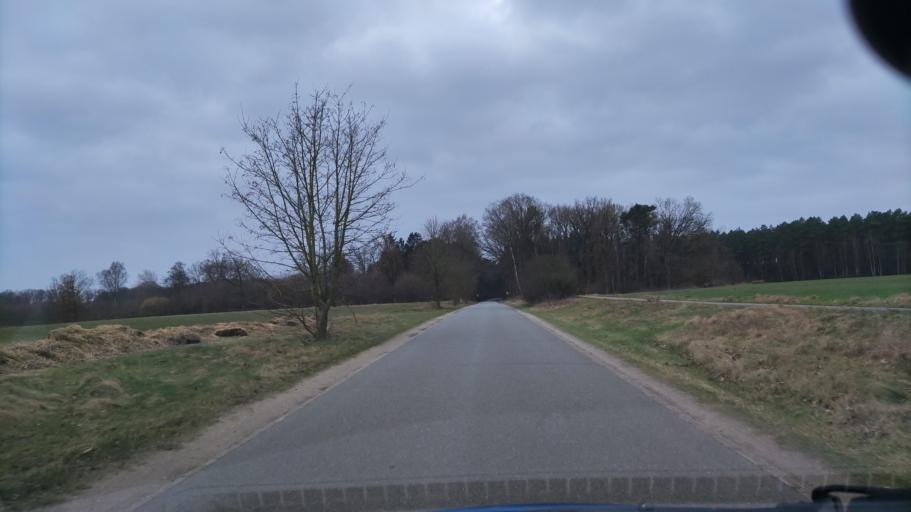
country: DE
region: Lower Saxony
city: Sudergellersen
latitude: 53.2141
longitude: 10.3288
